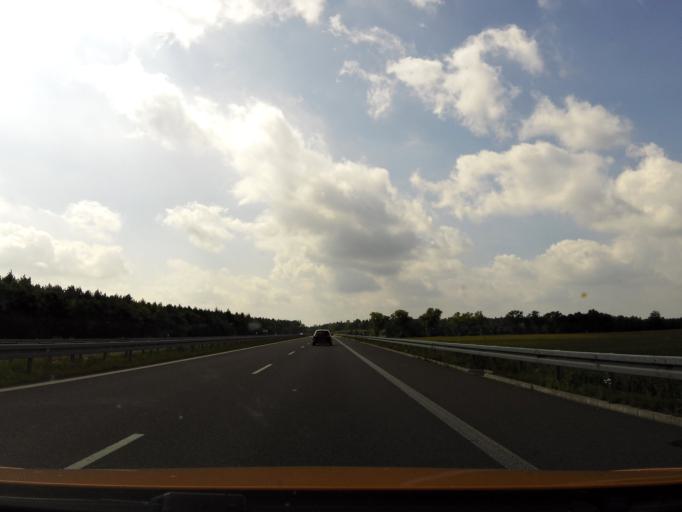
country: PL
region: West Pomeranian Voivodeship
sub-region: Powiat goleniowski
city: Nowogard
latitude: 53.6750
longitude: 15.0813
